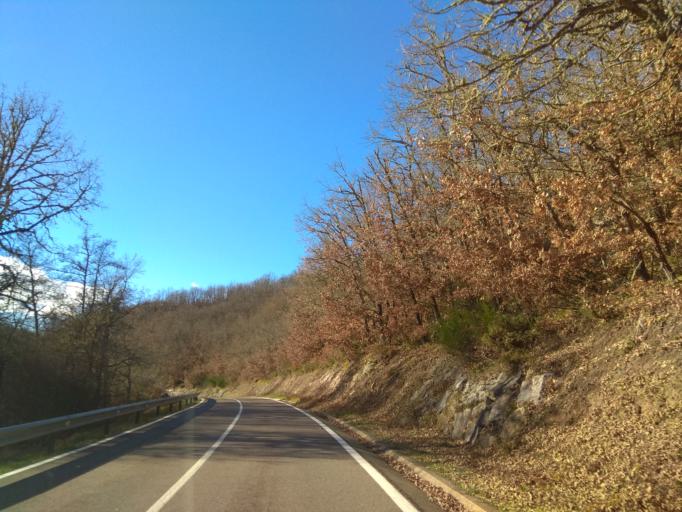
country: ES
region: Cantabria
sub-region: Provincia de Cantabria
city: San Martin de Elines
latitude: 42.9030
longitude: -3.8864
